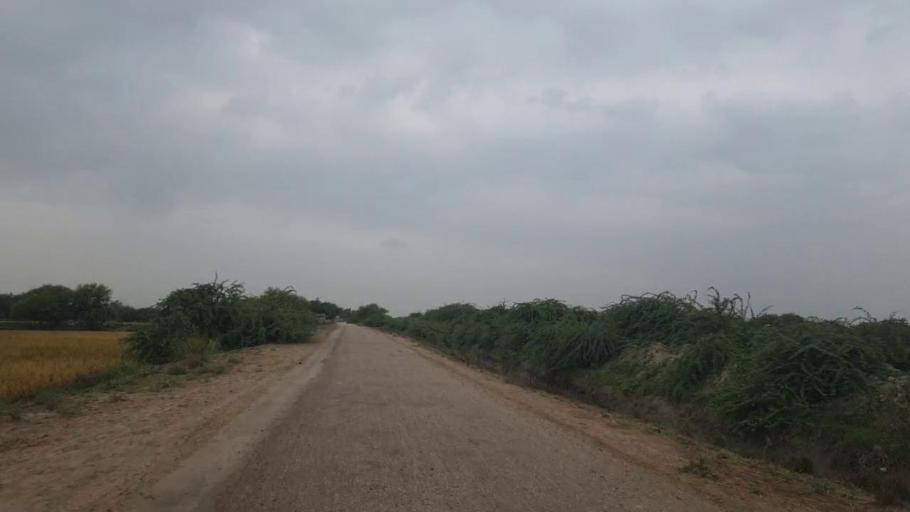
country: PK
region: Sindh
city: Badin
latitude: 24.6367
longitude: 68.6820
